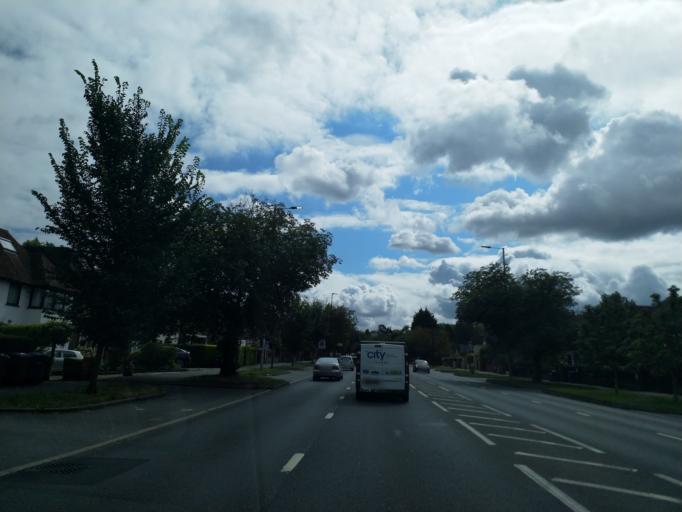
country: GB
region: England
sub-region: Greater London
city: Belsize Park
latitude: 51.5834
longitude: -0.1667
